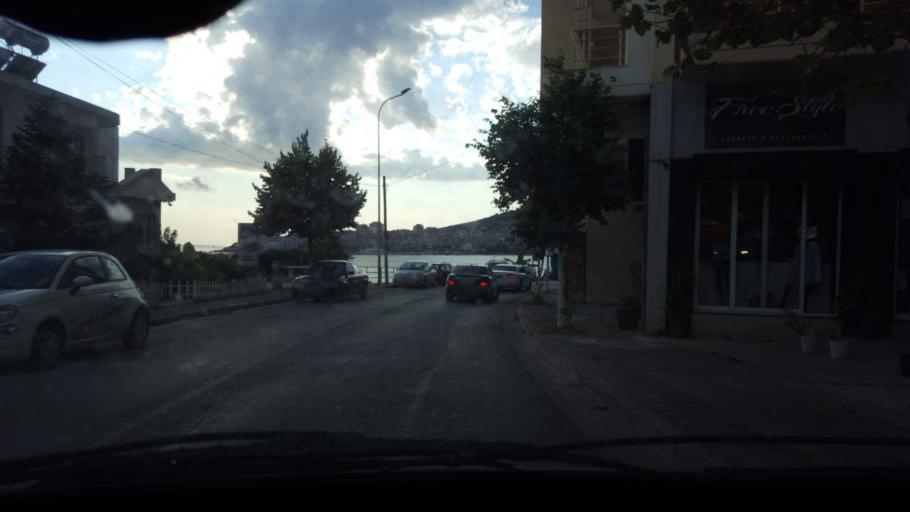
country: AL
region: Vlore
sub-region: Rrethi i Sarandes
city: Sarande
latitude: 39.8670
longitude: 20.0162
